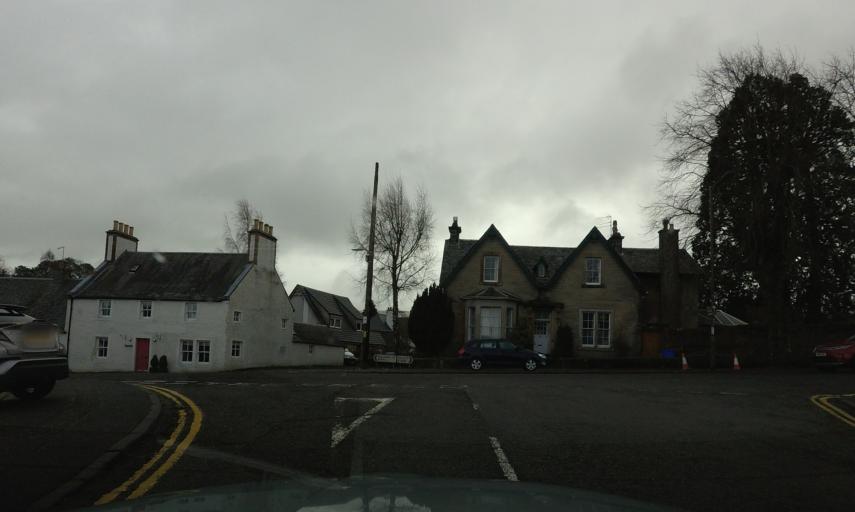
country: GB
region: Scotland
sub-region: Stirling
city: Callander
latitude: 56.1269
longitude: -4.1710
